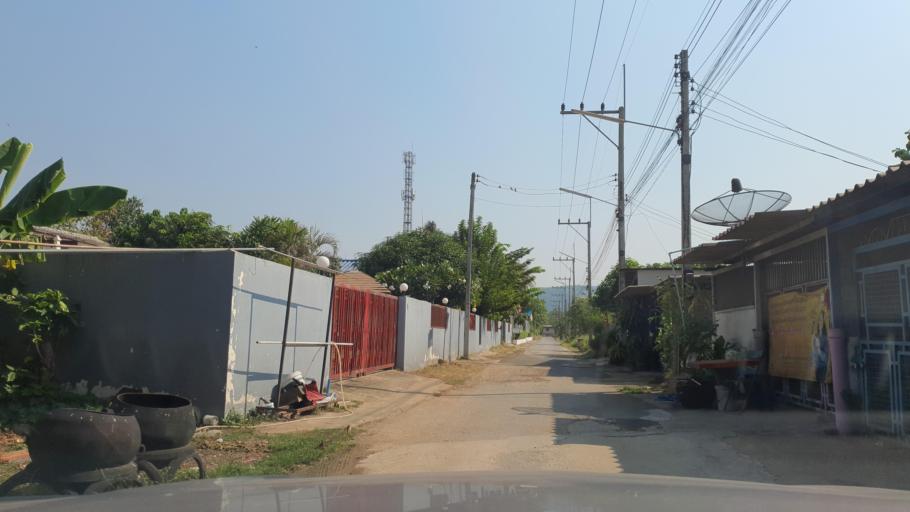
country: TH
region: Kanchanaburi
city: Kanchanaburi
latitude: 14.0326
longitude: 99.4951
